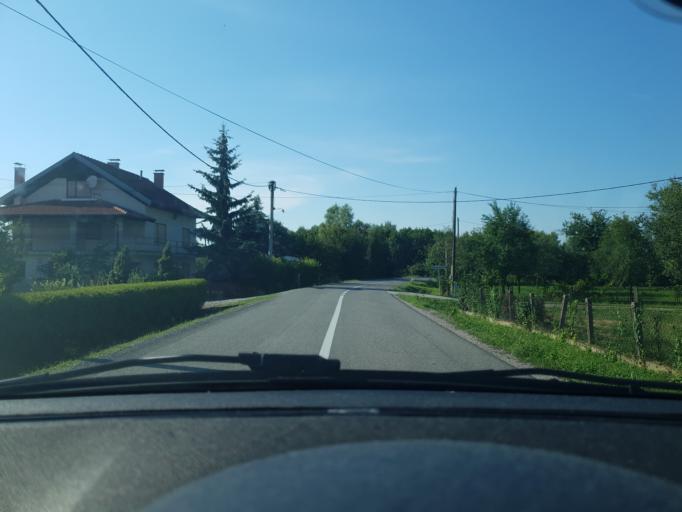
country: HR
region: Zagrebacka
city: Jakovlje
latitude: 45.9262
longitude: 15.8428
